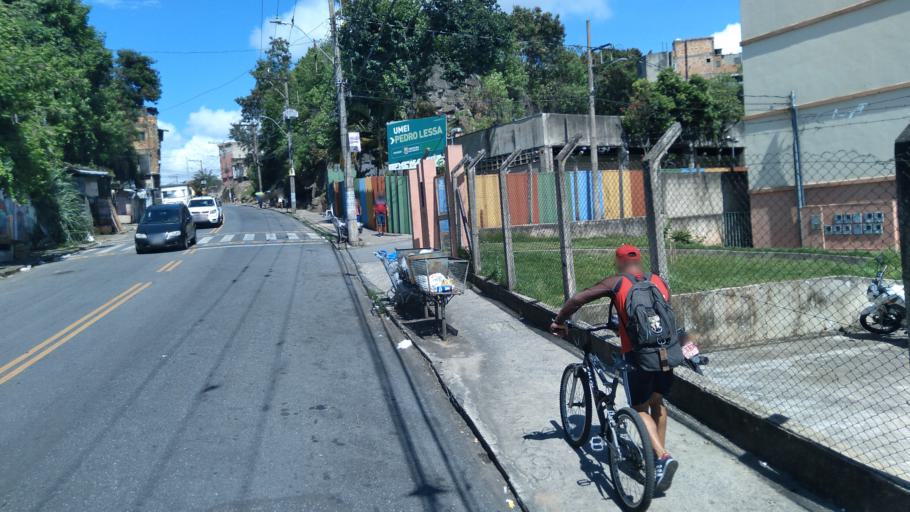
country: BR
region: Minas Gerais
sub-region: Belo Horizonte
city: Belo Horizonte
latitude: -19.9044
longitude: -43.9502
